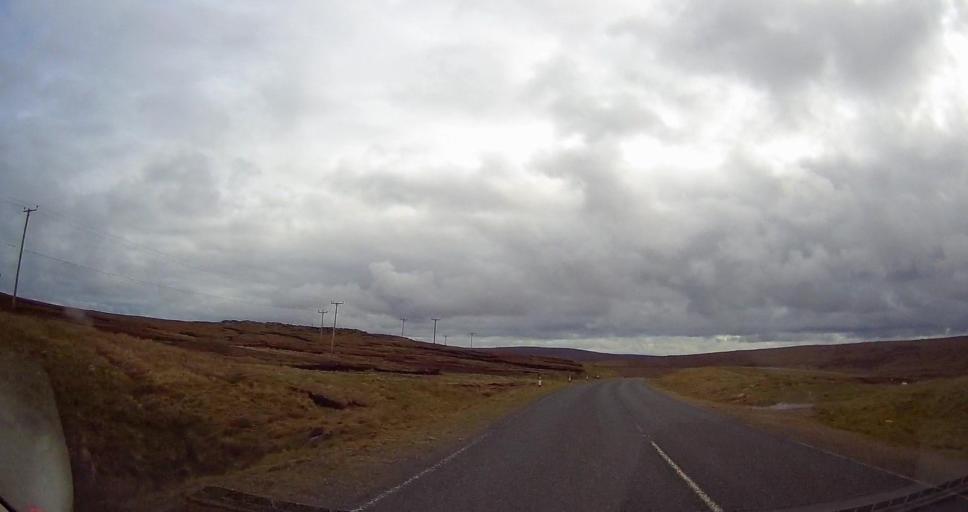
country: GB
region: Scotland
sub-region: Shetland Islands
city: Shetland
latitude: 60.5916
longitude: -1.1644
